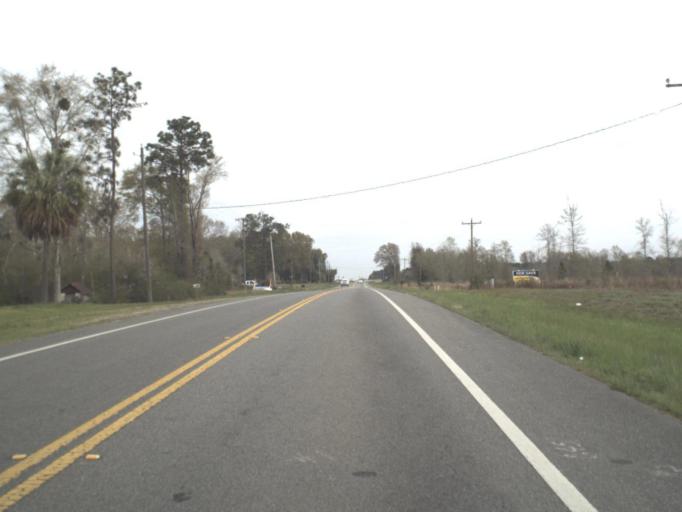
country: US
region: Florida
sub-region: Holmes County
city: Bonifay
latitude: 30.7510
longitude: -85.6850
